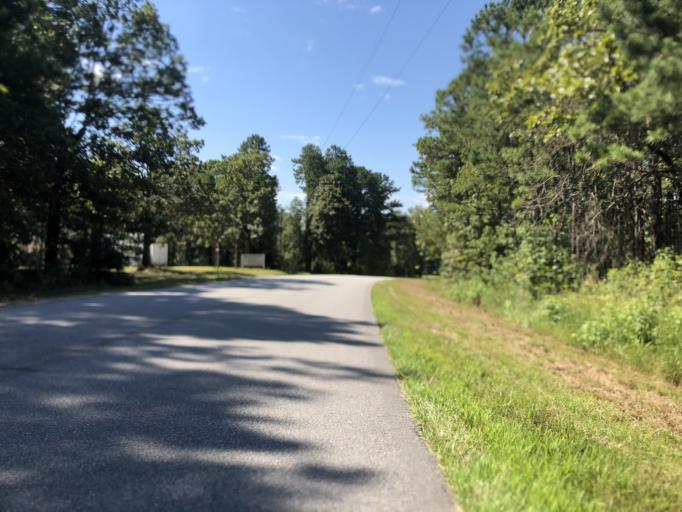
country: US
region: Georgia
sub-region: Heard County
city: Franklin
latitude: 33.3800
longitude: -85.0088
